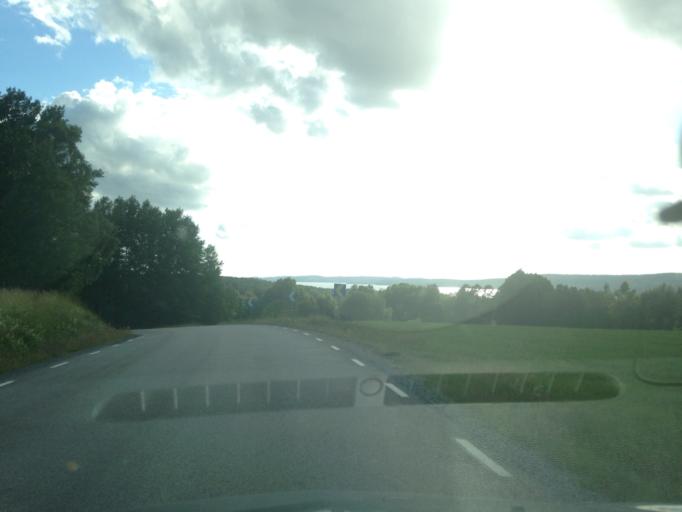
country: SE
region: Vaestra Goetaland
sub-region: Marks Kommun
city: Horred
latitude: 57.4758
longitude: 12.3992
